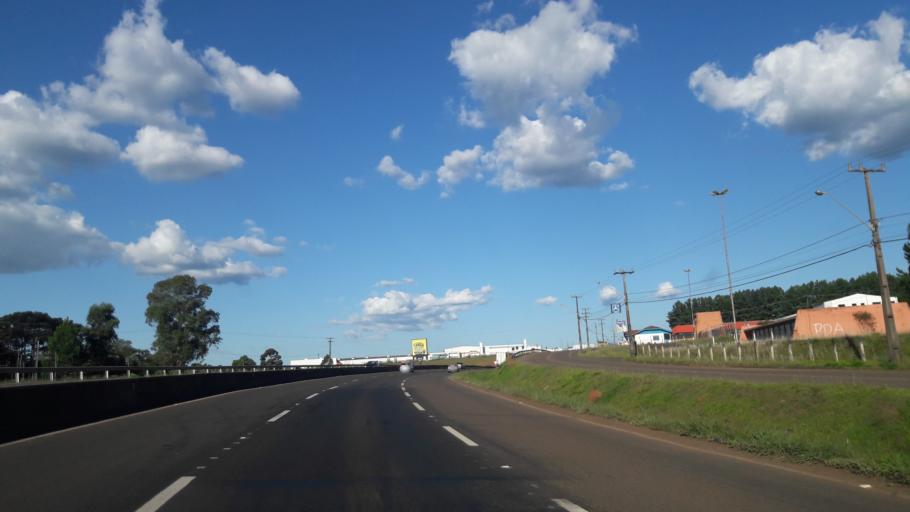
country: BR
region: Parana
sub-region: Guarapuava
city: Guarapuava
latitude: -25.3491
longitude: -51.4556
